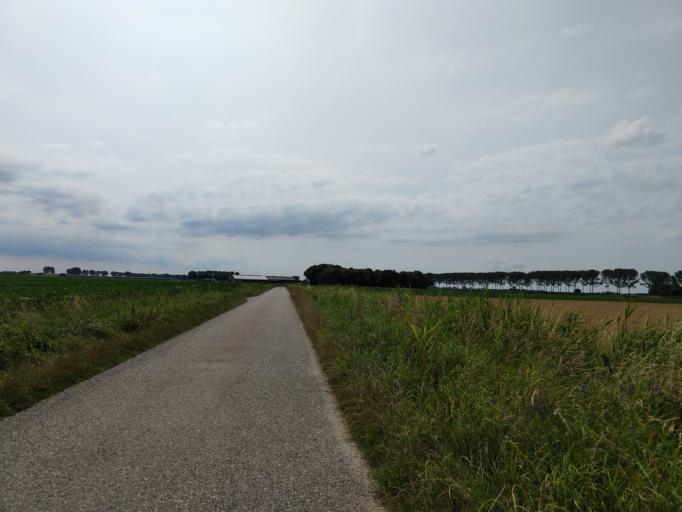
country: NL
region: North Brabant
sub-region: Gemeente Steenbergen
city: Dinteloord
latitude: 51.6723
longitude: 4.3334
